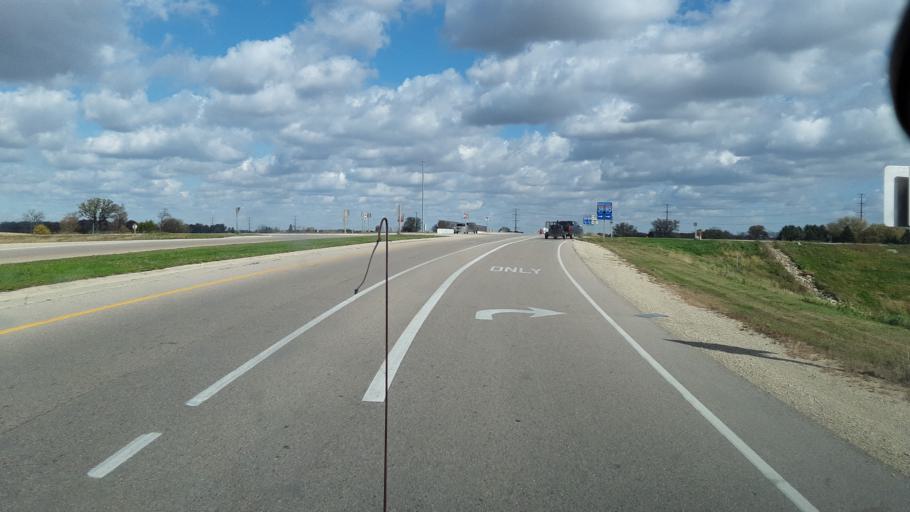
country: US
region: Wisconsin
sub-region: Rock County
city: Edgerton
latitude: 42.8716
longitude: -89.0572
